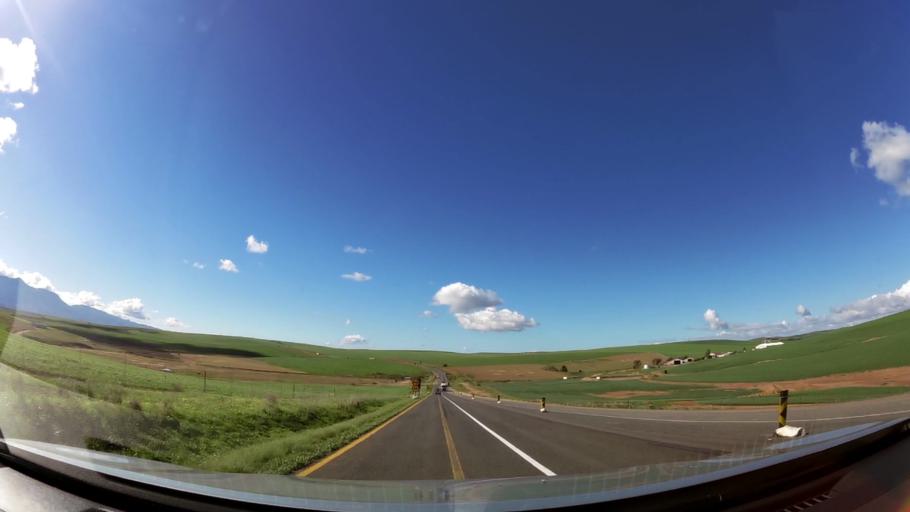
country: ZA
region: Western Cape
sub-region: Overberg District Municipality
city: Caledon
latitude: -34.1830
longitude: 19.6755
